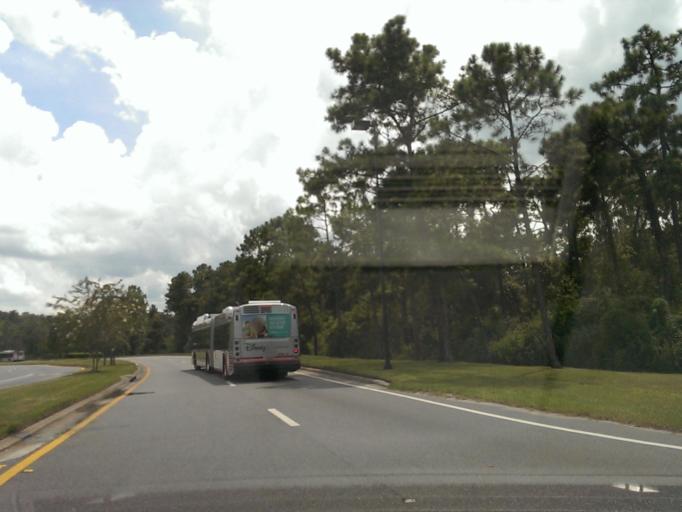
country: US
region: Florida
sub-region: Osceola County
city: Celebration
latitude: 28.3905
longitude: -81.5417
